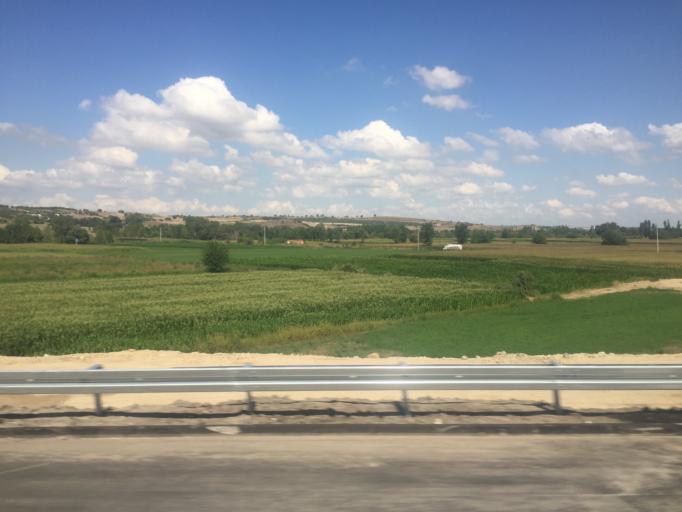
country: TR
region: Balikesir
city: Gobel
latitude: 39.9835
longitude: 28.1808
